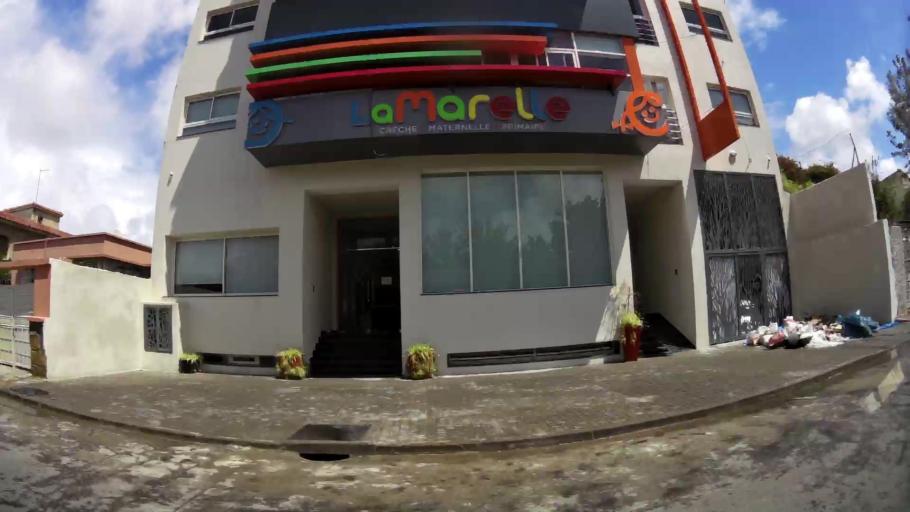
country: MA
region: Grand Casablanca
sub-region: Casablanca
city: Casablanca
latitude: 33.5698
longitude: -7.6412
